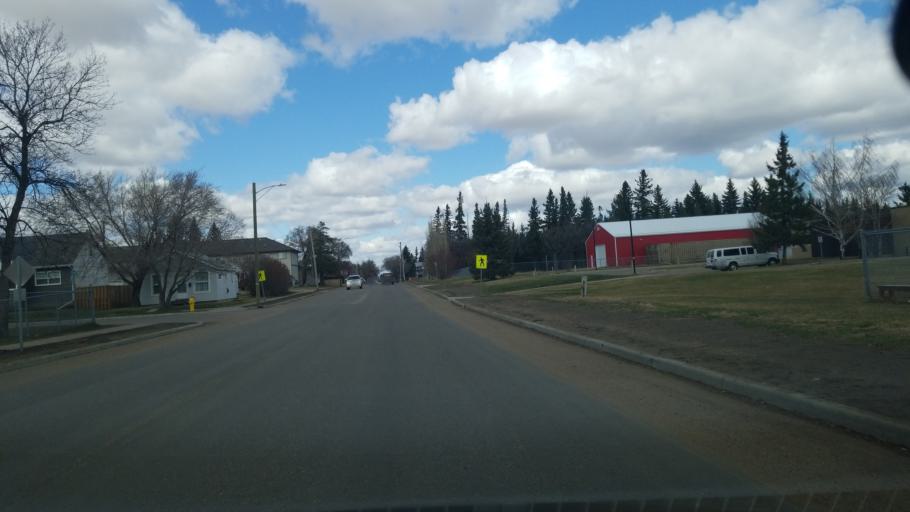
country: CA
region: Saskatchewan
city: Lloydminster
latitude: 53.2757
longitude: -109.9974
